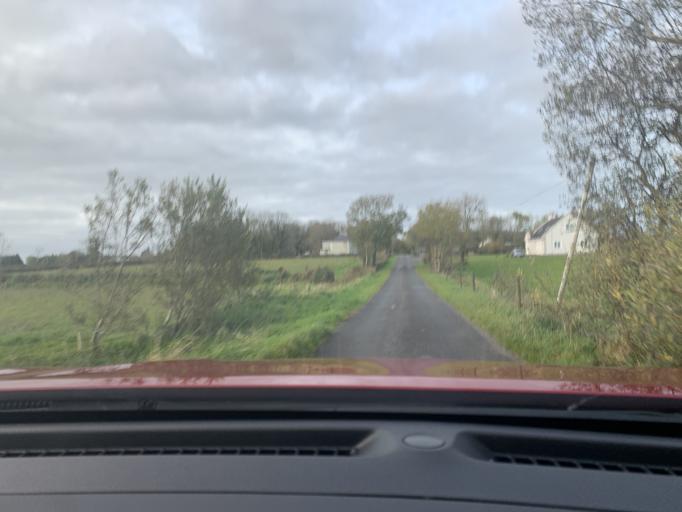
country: IE
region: Connaught
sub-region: Roscommon
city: Ballaghaderreen
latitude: 54.0092
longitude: -8.6073
